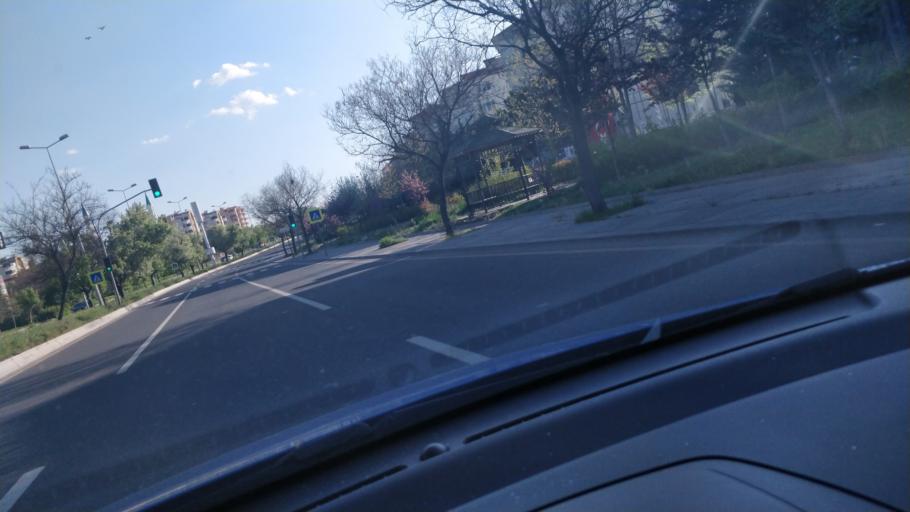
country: TR
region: Ankara
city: Batikent
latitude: 39.9563
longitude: 32.7194
